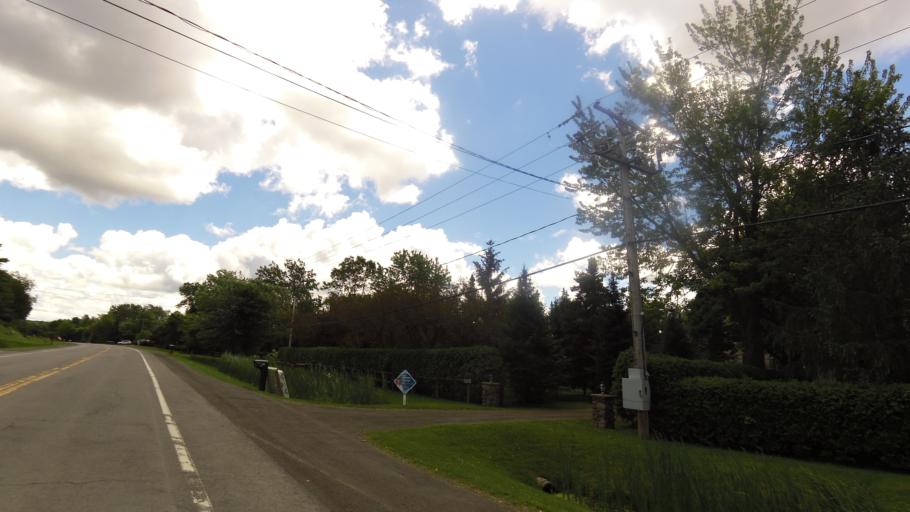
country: CA
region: Quebec
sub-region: Monteregie
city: Rigaud
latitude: 45.5311
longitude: -74.2392
